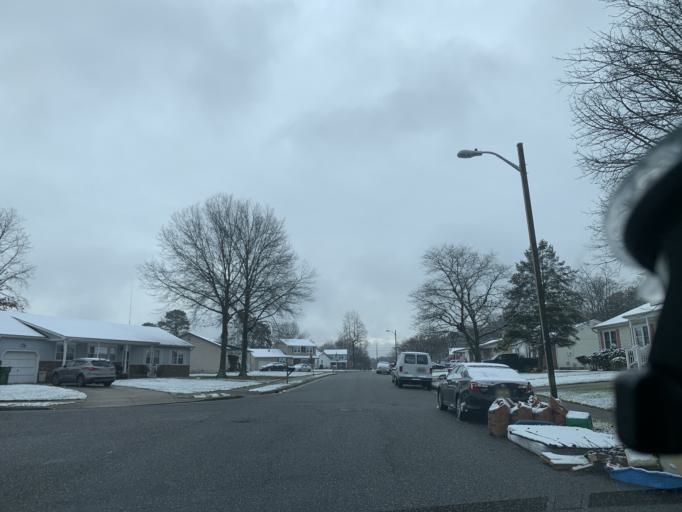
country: US
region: New Jersey
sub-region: Atlantic County
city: Pomona
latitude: 39.4312
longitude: -74.5929
